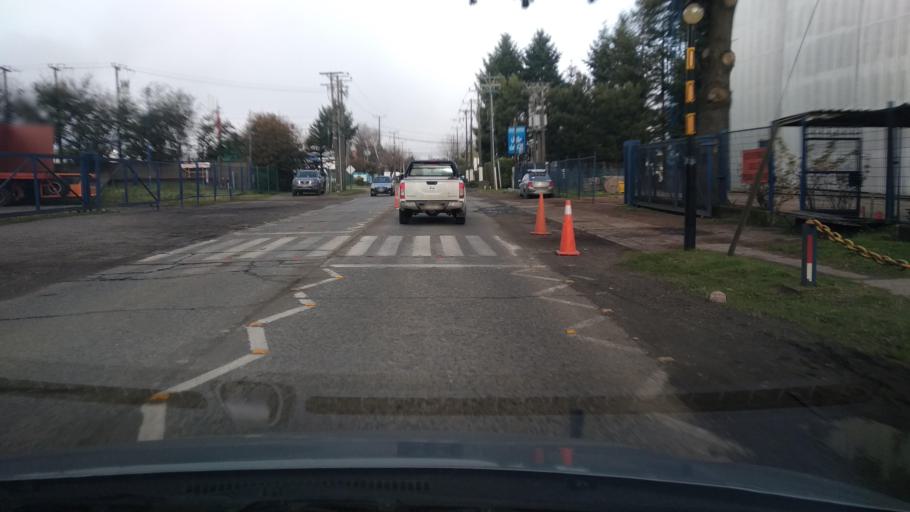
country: CL
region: Los Rios
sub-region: Provincia de Valdivia
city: Valdivia
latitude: -39.8066
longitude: -73.2367
